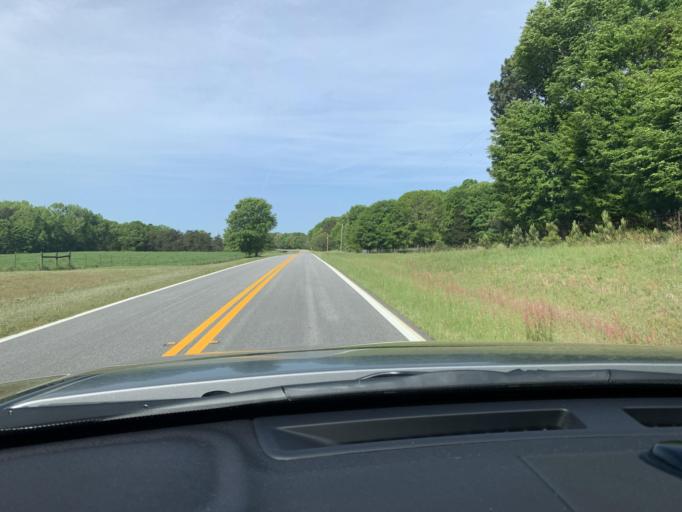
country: US
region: Georgia
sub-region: Oconee County
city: Watkinsville
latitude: 33.8156
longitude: -83.3906
